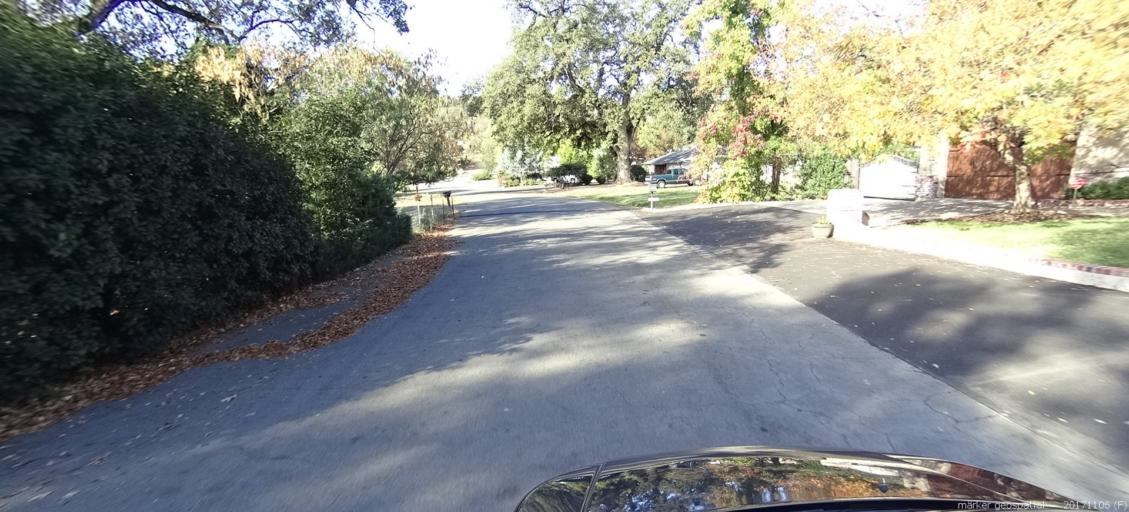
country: US
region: California
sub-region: Shasta County
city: Palo Cedro
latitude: 40.5417
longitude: -122.2462
